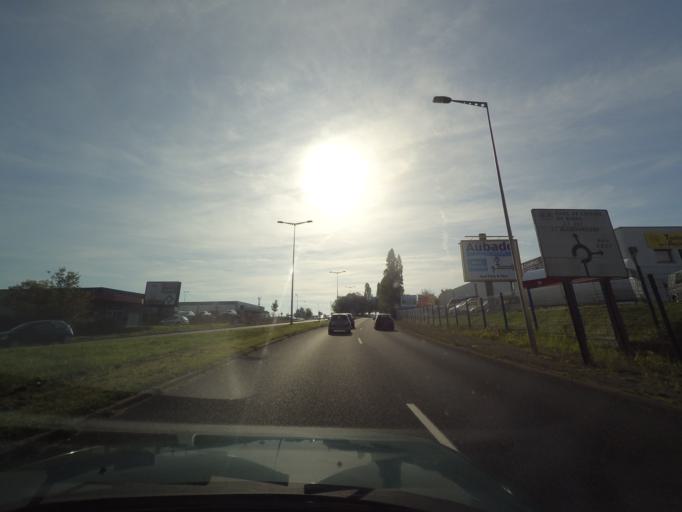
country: FR
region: Pays de la Loire
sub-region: Departement de Maine-et-Loire
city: Cholet
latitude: 47.0709
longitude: -0.8547
